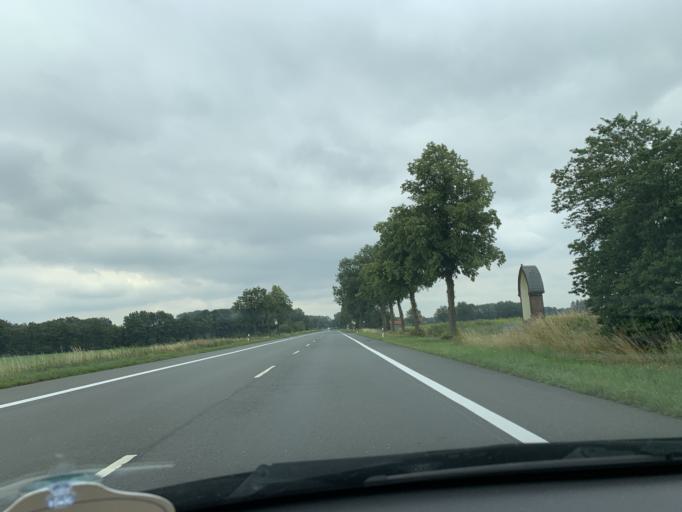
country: DE
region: North Rhine-Westphalia
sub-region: Regierungsbezirk Munster
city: Ennigerloh
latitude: 51.9088
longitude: 8.0475
